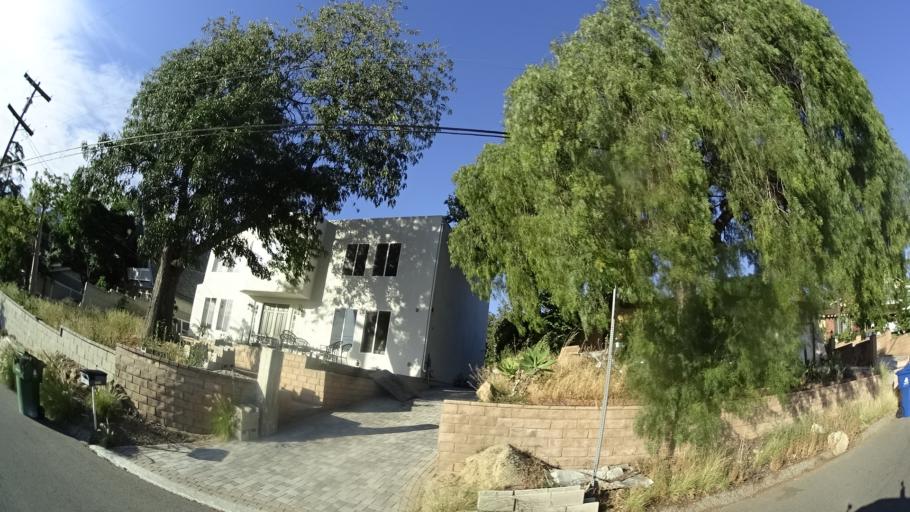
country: US
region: California
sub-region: Los Angeles County
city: La Crescenta-Montrose
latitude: 34.2703
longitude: -118.3005
